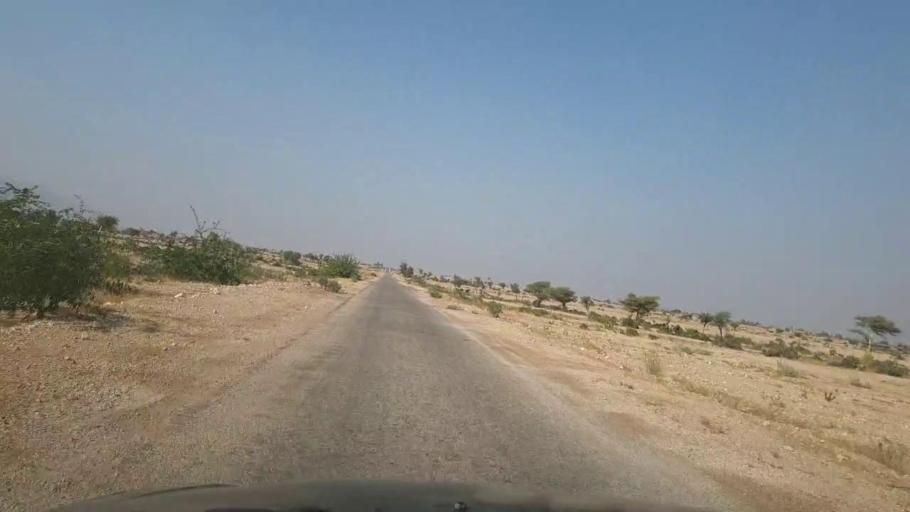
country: PK
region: Sindh
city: Jamshoro
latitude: 25.5951
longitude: 67.8175
